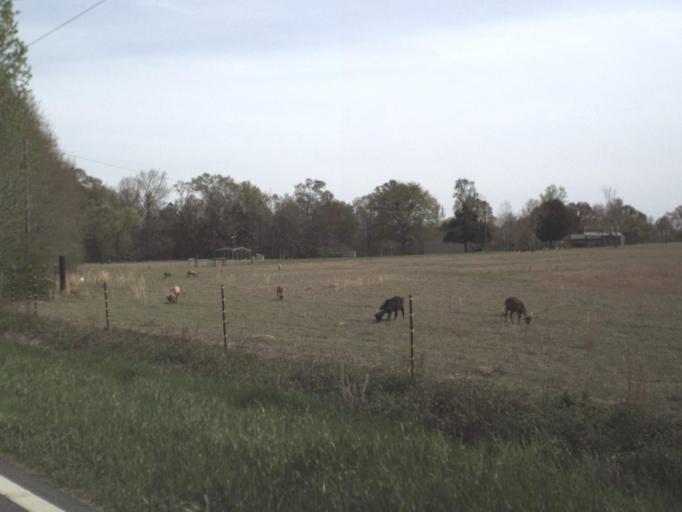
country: US
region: Florida
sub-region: Jackson County
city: Graceville
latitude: 30.9531
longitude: -85.4529
